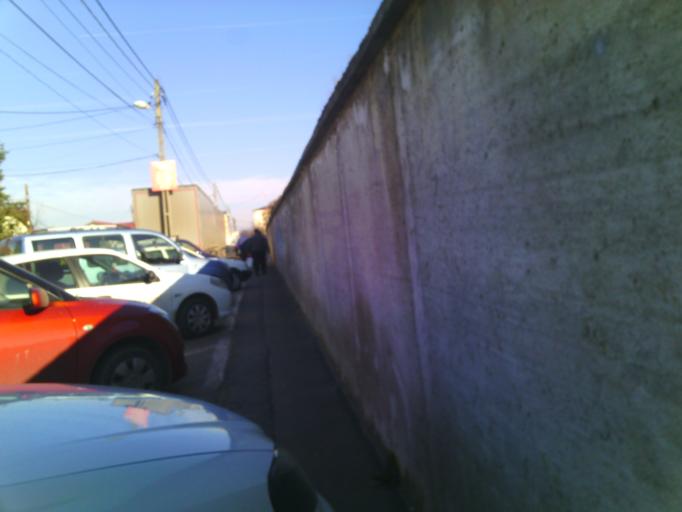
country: RO
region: Ilfov
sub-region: Comuna Popesti-Leordeni
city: Popesti-Leordeni
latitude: 44.3832
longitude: 26.1611
